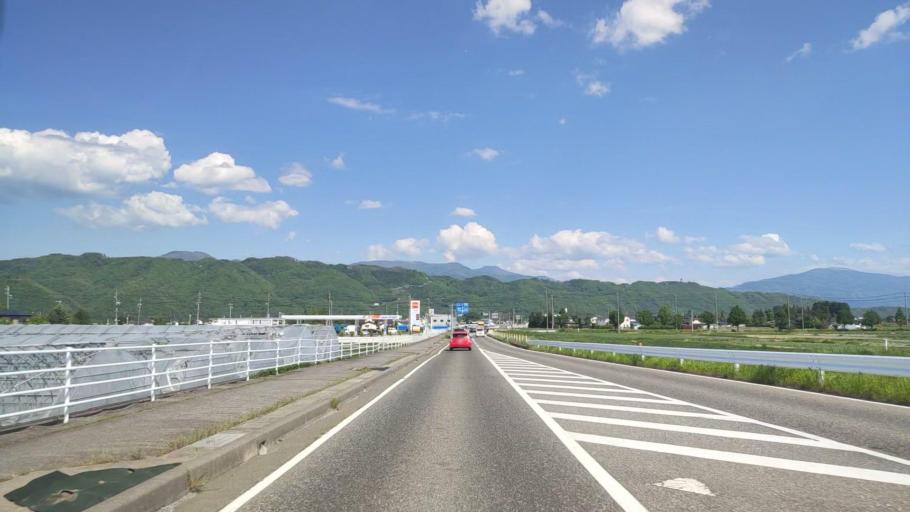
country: JP
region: Nagano
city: Toyoshina
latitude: 36.2804
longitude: 137.9182
